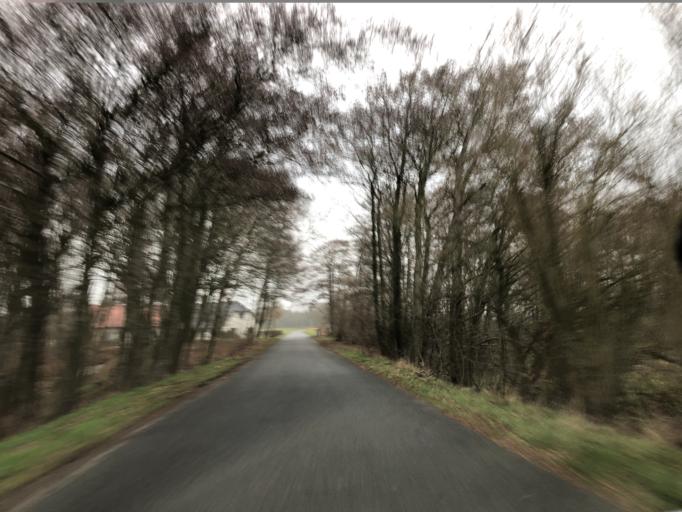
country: DK
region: Central Jutland
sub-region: Holstebro Kommune
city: Ulfborg
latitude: 56.2006
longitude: 8.3137
